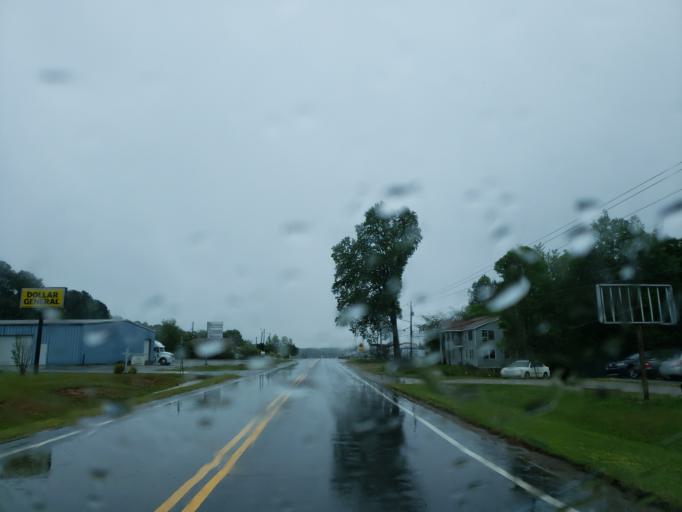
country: US
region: Georgia
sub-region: Haralson County
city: Bremen
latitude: 33.7237
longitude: -85.1299
